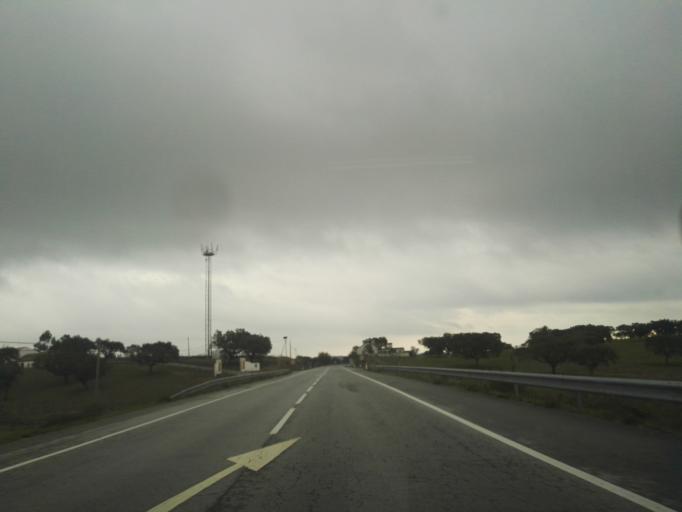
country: PT
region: Portalegre
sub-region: Portalegre
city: Urra
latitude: 39.2075
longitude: -7.3715
